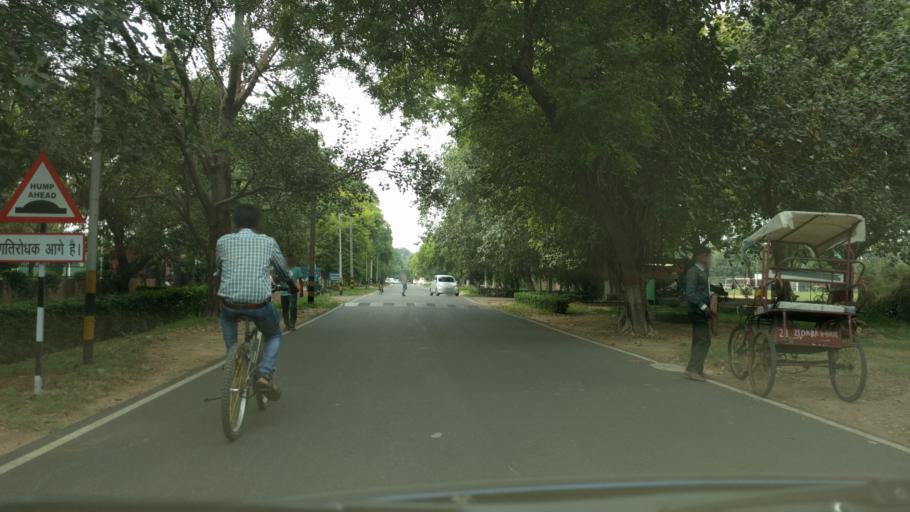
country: IN
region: NCT
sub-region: Central Delhi
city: Karol Bagh
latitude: 28.6344
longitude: 77.1616
